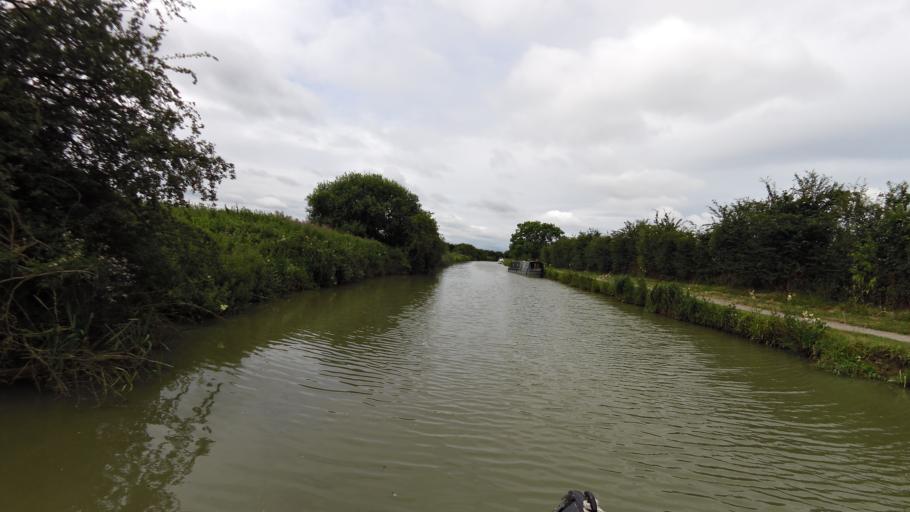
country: GB
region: England
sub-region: Wiltshire
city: Seend
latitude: 51.3491
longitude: -2.1173
